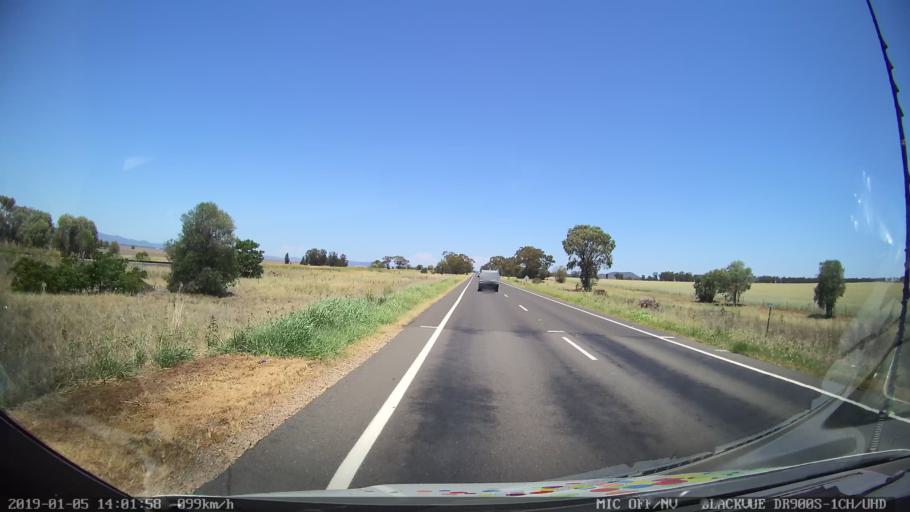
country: AU
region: New South Wales
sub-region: Gunnedah
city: Gunnedah
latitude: -31.1751
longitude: 150.3319
